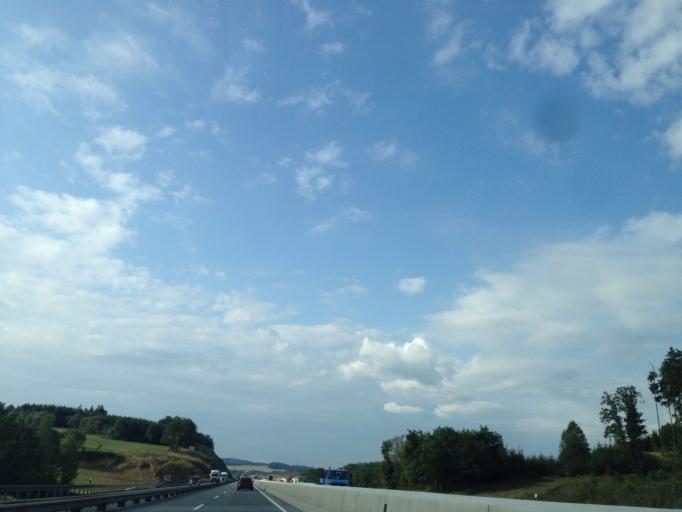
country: DE
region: Thuringia
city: Gorkwitz
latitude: 50.5992
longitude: 11.7872
